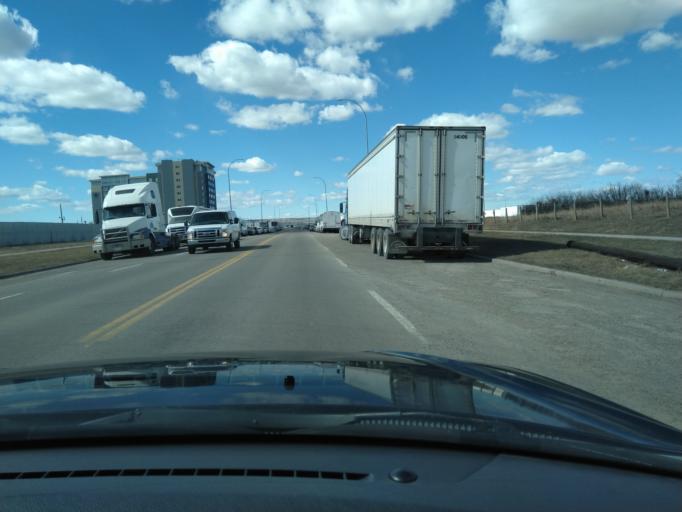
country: CA
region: Alberta
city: Calgary
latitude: 51.1434
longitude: -114.0080
